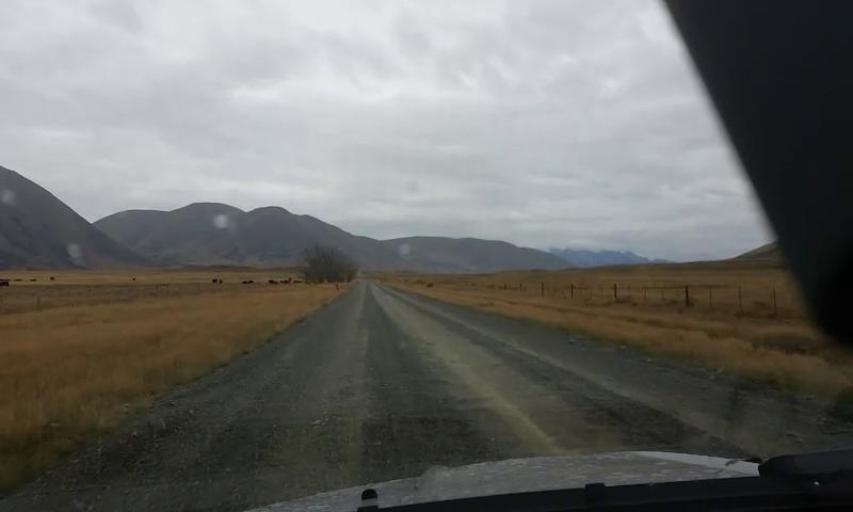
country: NZ
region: Canterbury
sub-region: Ashburton District
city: Methven
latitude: -43.6143
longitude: 171.1153
